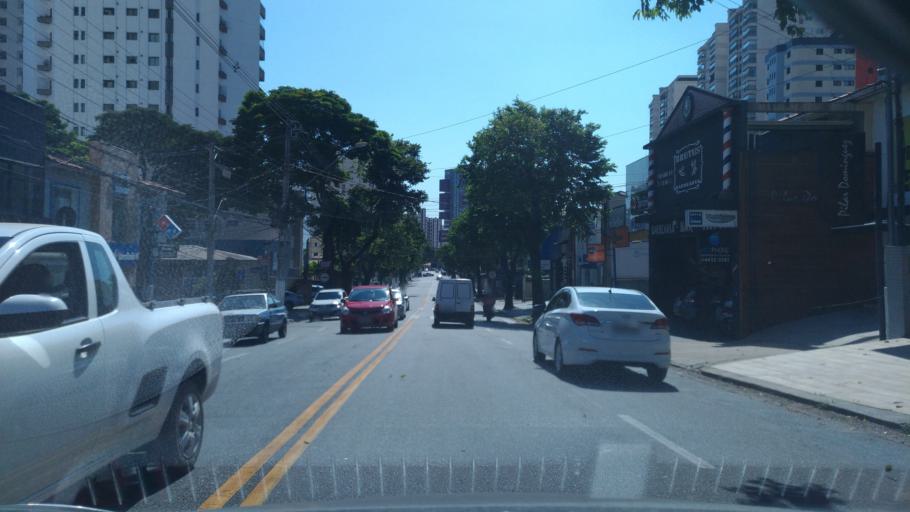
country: BR
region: Sao Paulo
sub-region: Santo Andre
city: Santo Andre
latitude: -23.6684
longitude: -46.5375
